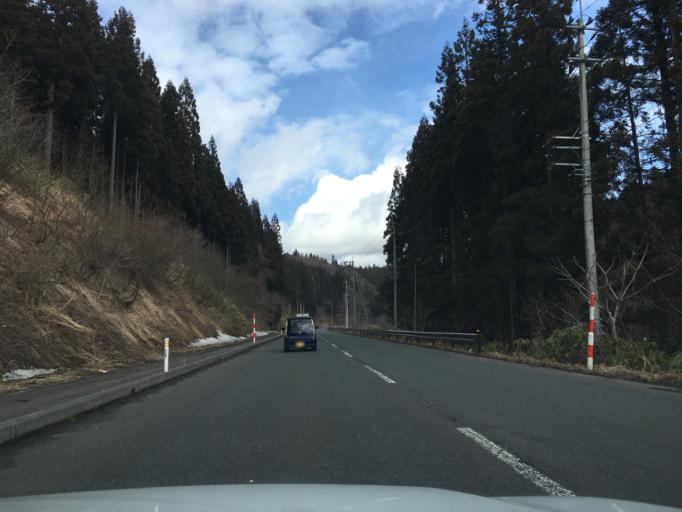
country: JP
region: Akita
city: Takanosu
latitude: 40.0950
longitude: 140.3410
